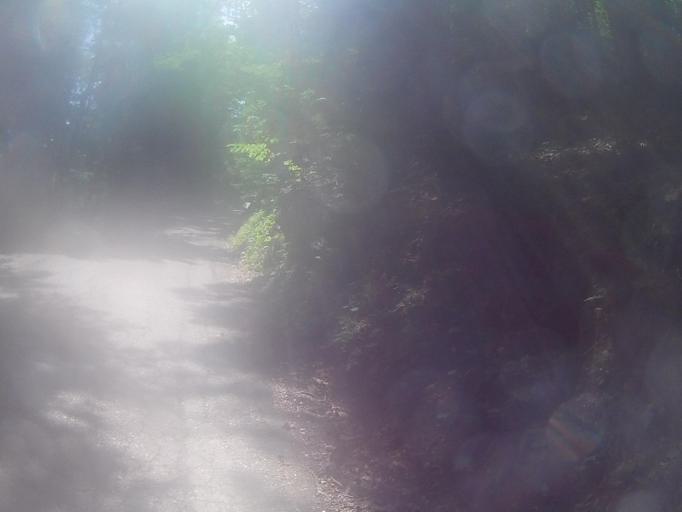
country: SI
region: Maribor
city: Bresternica
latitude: 46.6053
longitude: 15.5612
